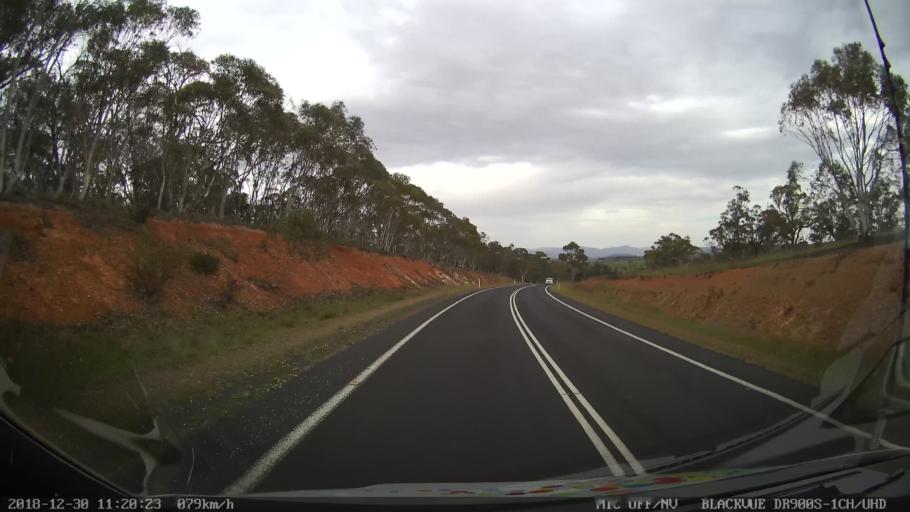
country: AU
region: New South Wales
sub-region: Snowy River
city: Jindabyne
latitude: -36.5188
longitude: 148.6893
